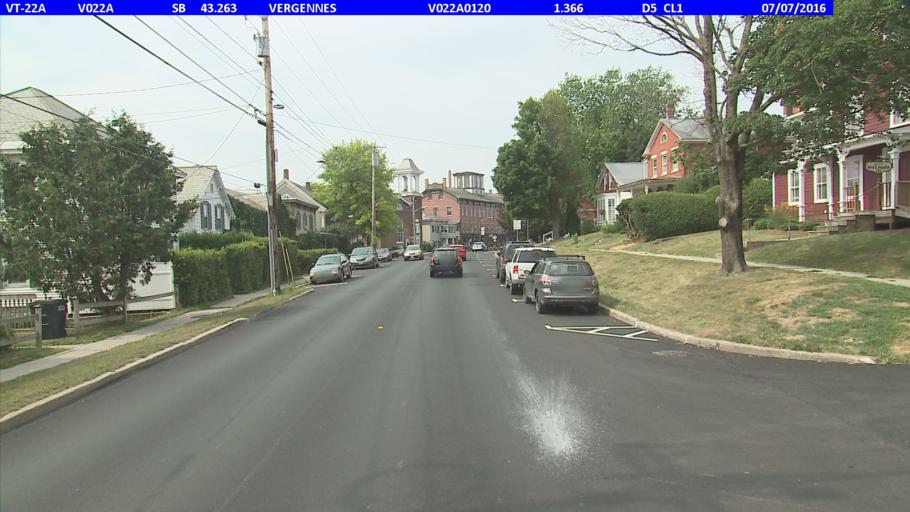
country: US
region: Vermont
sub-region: Addison County
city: Vergennes
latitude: 44.1692
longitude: -73.2500
